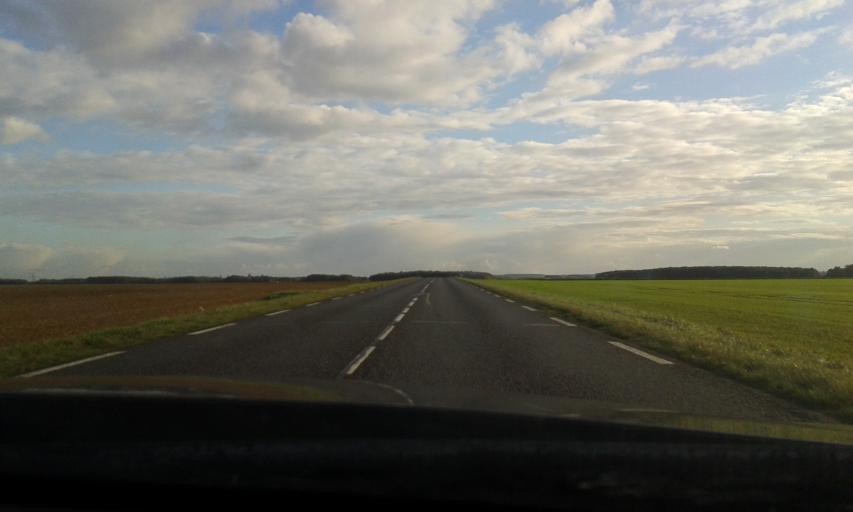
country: FR
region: Centre
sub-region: Departement d'Eure-et-Loir
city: Vernouillet
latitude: 48.7020
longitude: 1.3737
